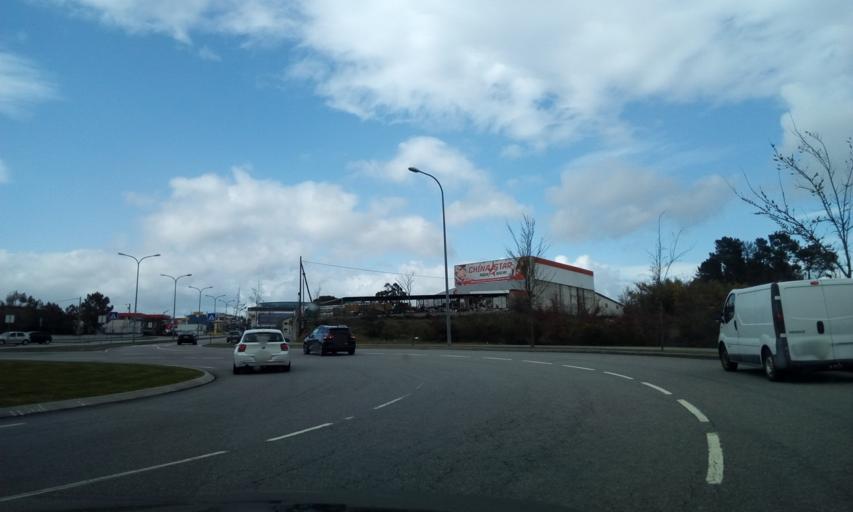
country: PT
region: Viseu
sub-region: Viseu
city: Viseu
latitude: 40.6339
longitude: -7.9050
